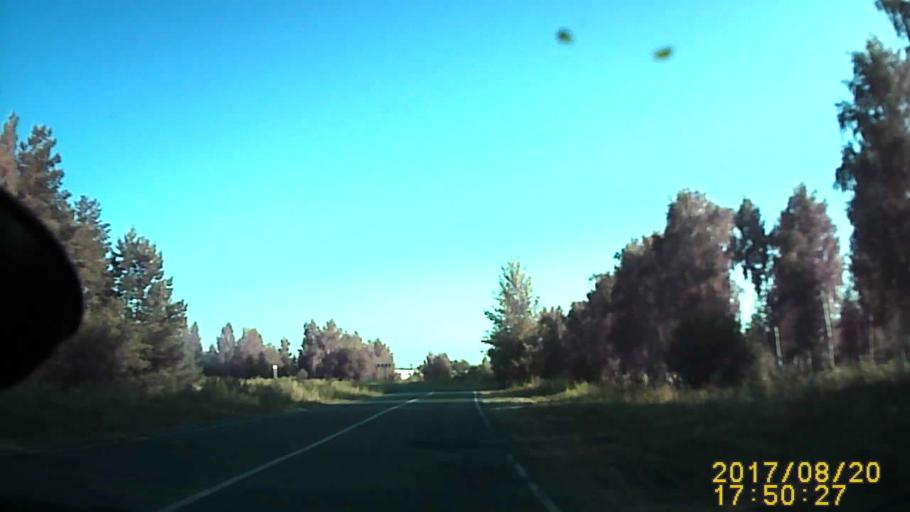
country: RU
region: Ulyanovsk
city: Cherdakly
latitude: 54.4302
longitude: 48.8077
